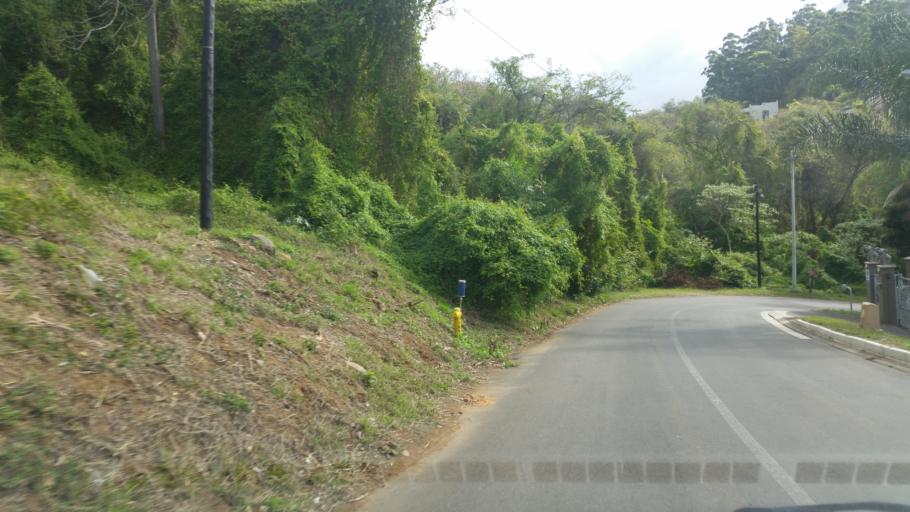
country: ZA
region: KwaZulu-Natal
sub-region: eThekwini Metropolitan Municipality
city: Berea
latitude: -29.8281
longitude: 30.9483
